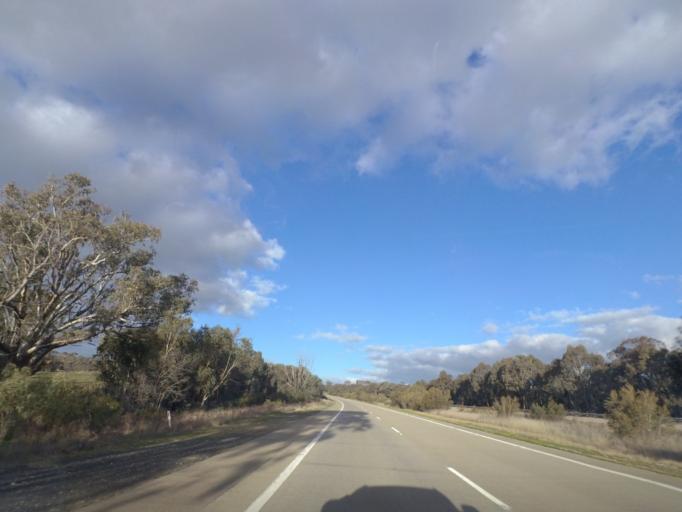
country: AU
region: New South Wales
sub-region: Yass Valley
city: Yass
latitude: -34.8016
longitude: 148.5429
